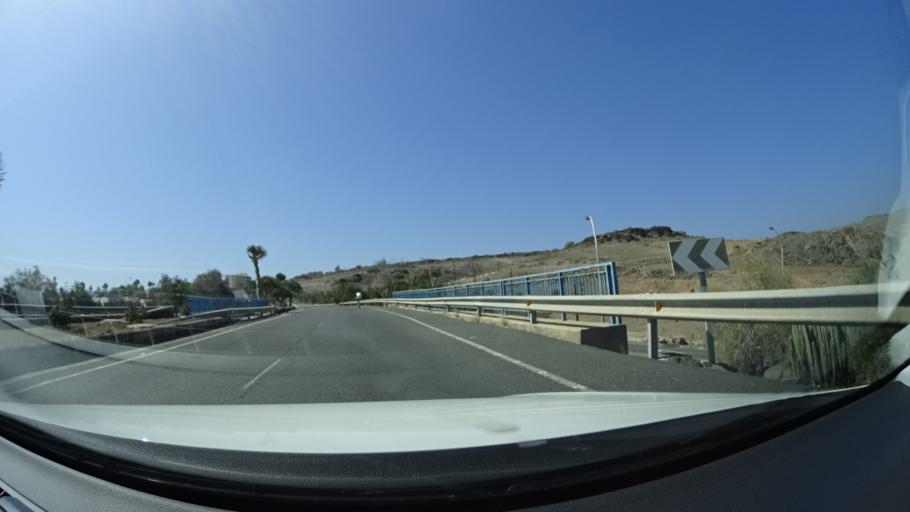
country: ES
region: Canary Islands
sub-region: Provincia de Las Palmas
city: Playa del Ingles
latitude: 27.7774
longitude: -15.5287
